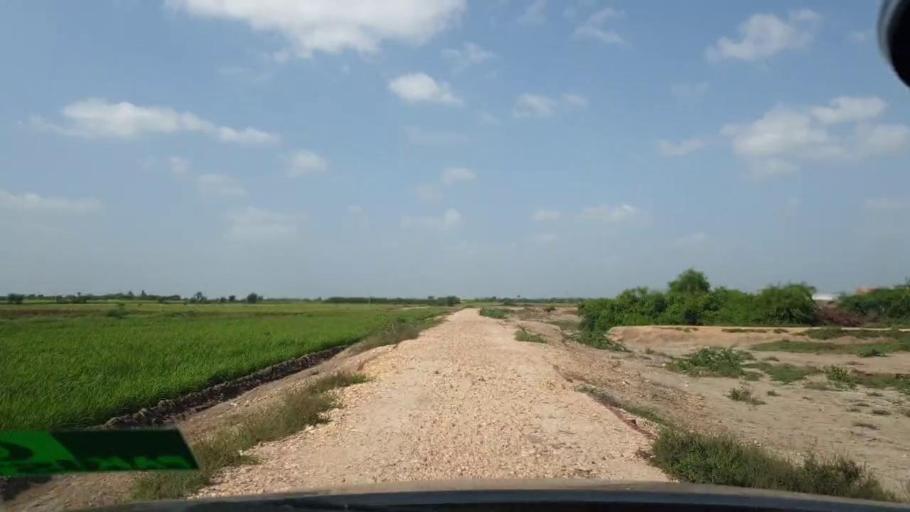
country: PK
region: Sindh
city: Tando Bago
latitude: 24.6645
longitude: 69.2040
